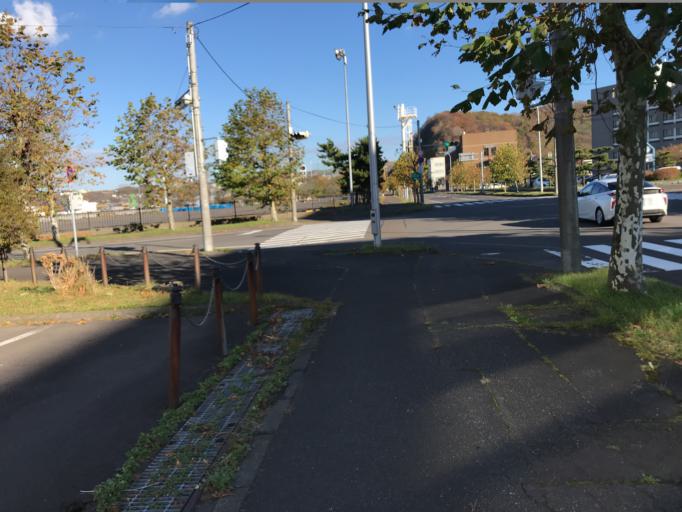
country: JP
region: Hokkaido
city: Muroran
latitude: 42.3229
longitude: 140.9718
